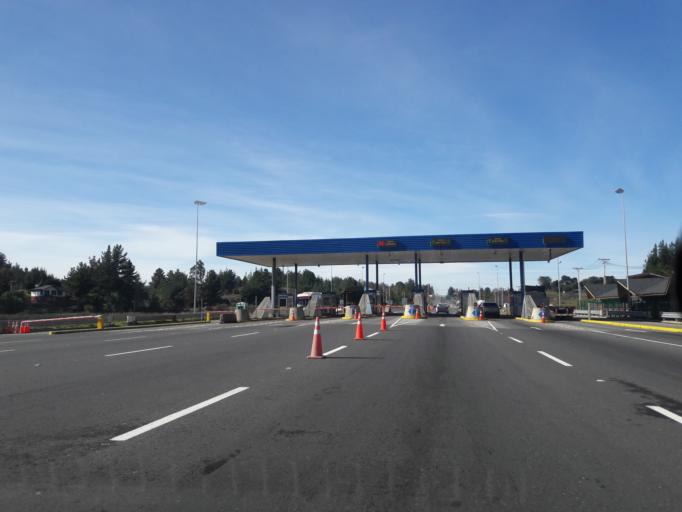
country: CL
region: Biobio
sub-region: Provincia de Biobio
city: Yumbel
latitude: -36.9603
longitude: -72.7291
